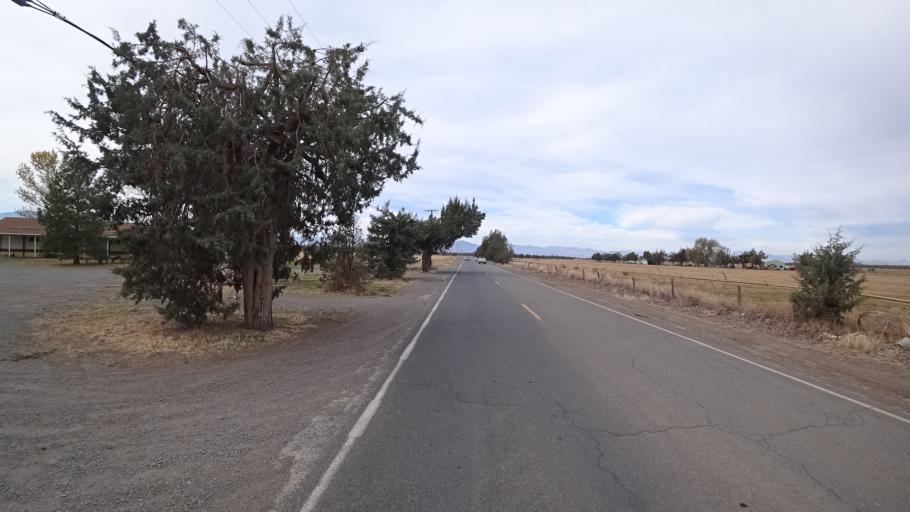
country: US
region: California
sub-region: Siskiyou County
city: Weed
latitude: 41.5956
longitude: -122.3314
